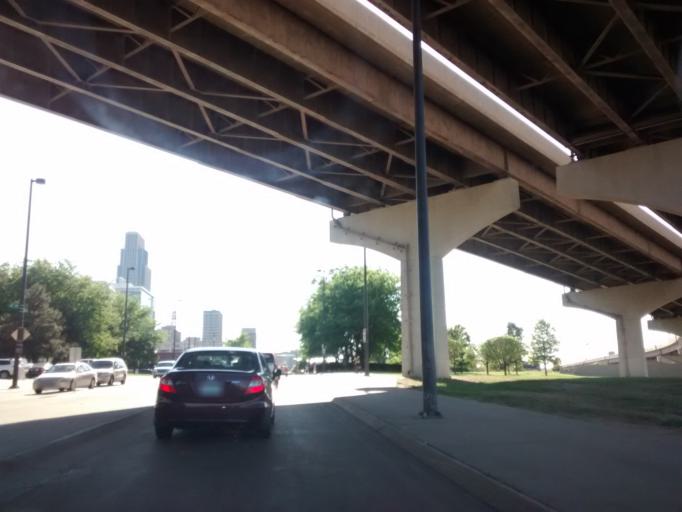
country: US
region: Nebraska
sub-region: Douglas County
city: Omaha
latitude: 41.2606
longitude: -95.9271
